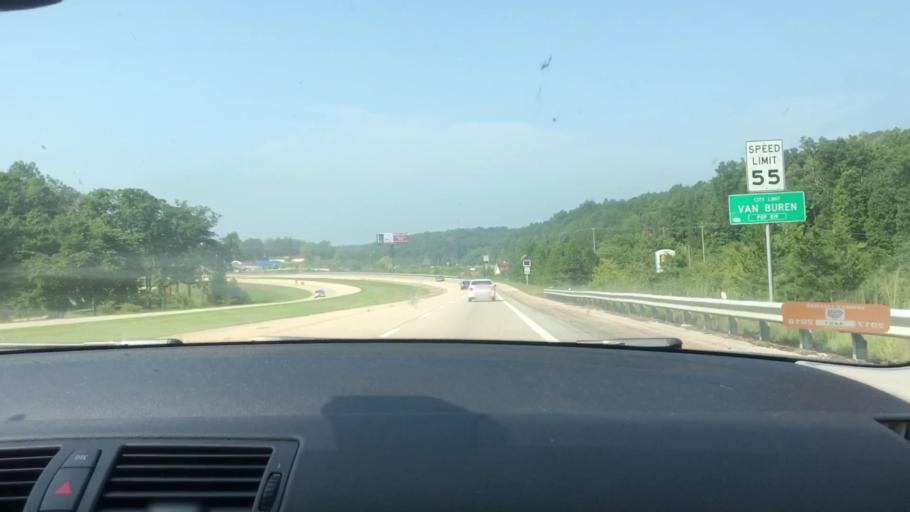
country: US
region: Missouri
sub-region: Carter County
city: Van Buren
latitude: 37.0143
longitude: -90.9891
